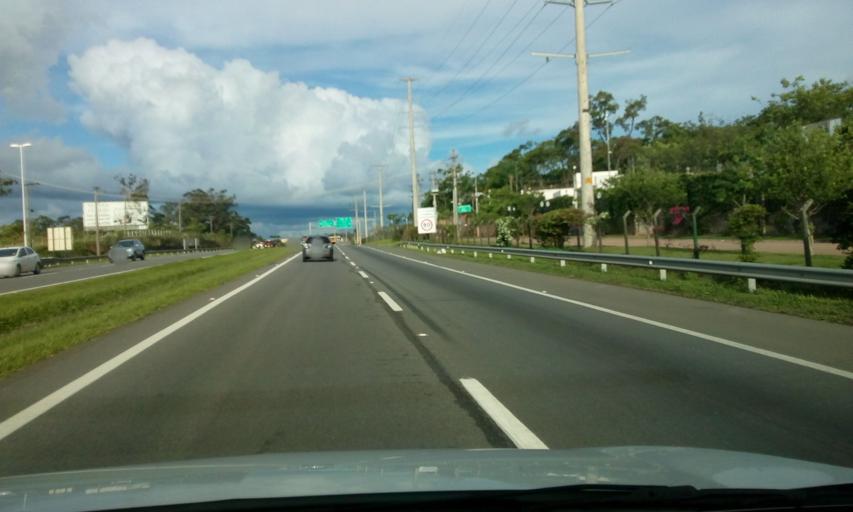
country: BR
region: Sao Paulo
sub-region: Jundiai
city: Jundiai
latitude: -23.1549
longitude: -46.8842
